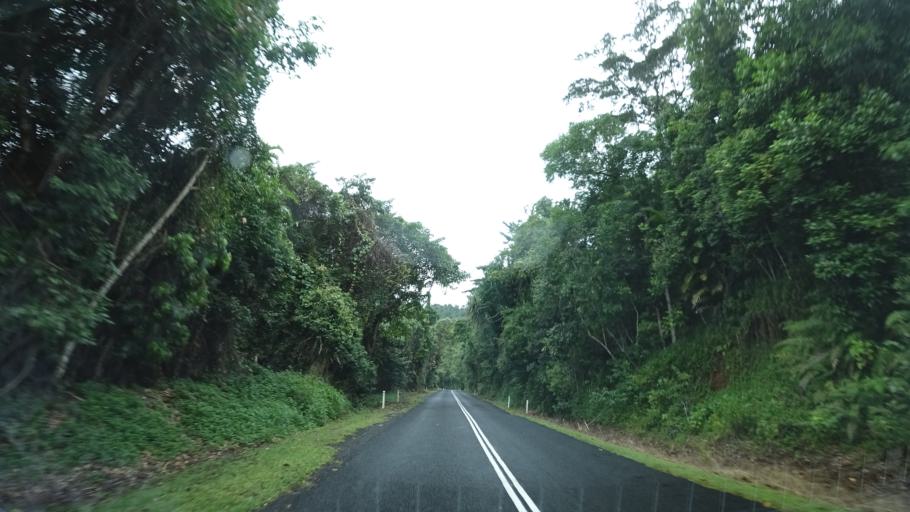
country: AU
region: Queensland
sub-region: Cassowary Coast
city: Innisfail
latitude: -17.5579
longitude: 146.0888
